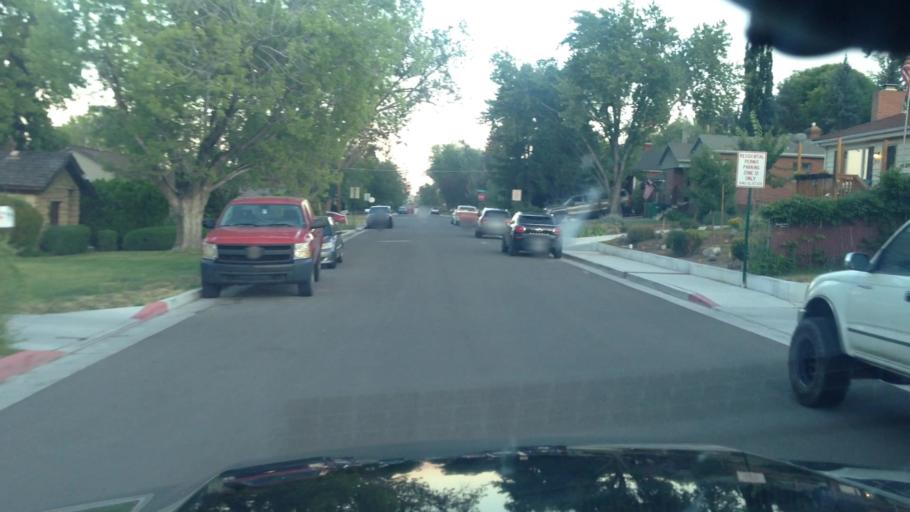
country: US
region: Nevada
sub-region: Washoe County
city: Reno
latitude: 39.5442
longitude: -119.8205
